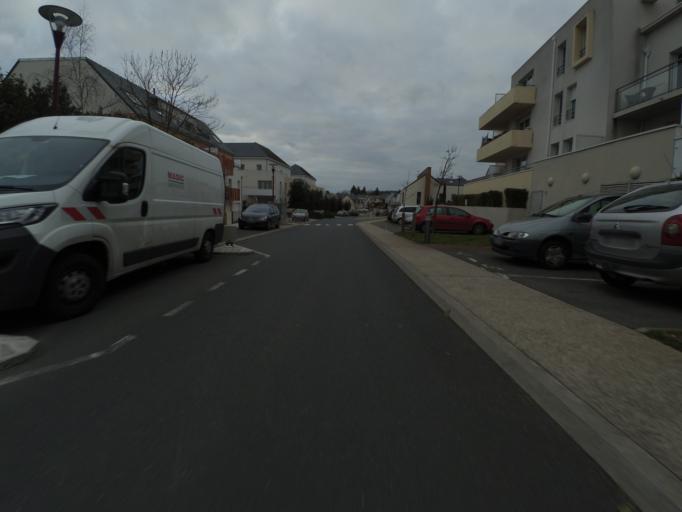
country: FR
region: Pays de la Loire
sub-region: Departement de la Loire-Atlantique
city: Carquefou
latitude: 47.3067
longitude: -1.4842
